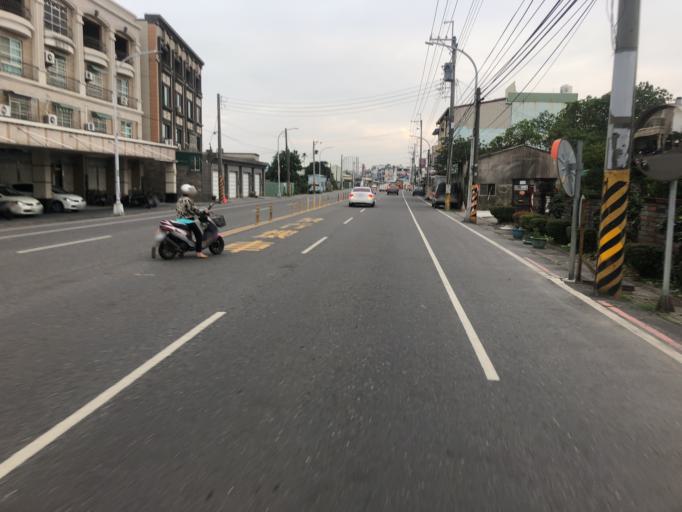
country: TW
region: Taiwan
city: Xinying
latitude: 23.1413
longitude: 120.2882
